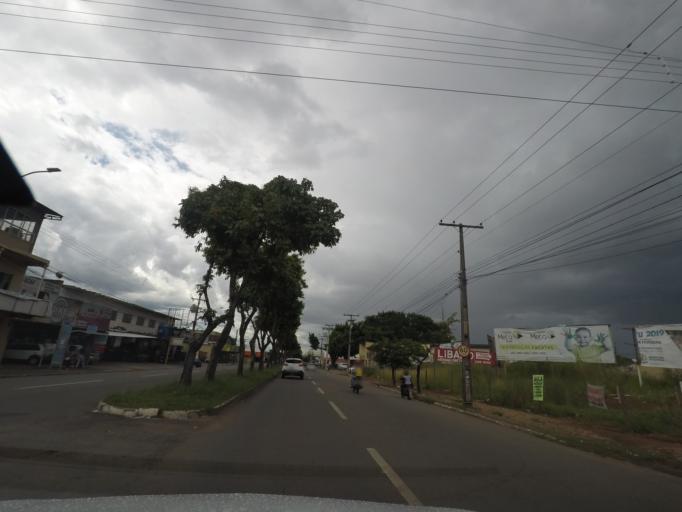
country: BR
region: Goias
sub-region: Goiania
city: Goiania
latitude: -16.7247
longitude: -49.3226
